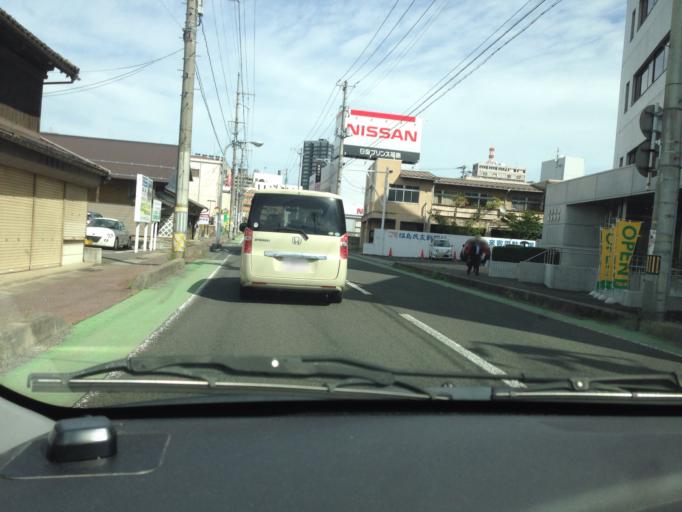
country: JP
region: Fukushima
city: Fukushima-shi
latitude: 37.7468
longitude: 140.4644
